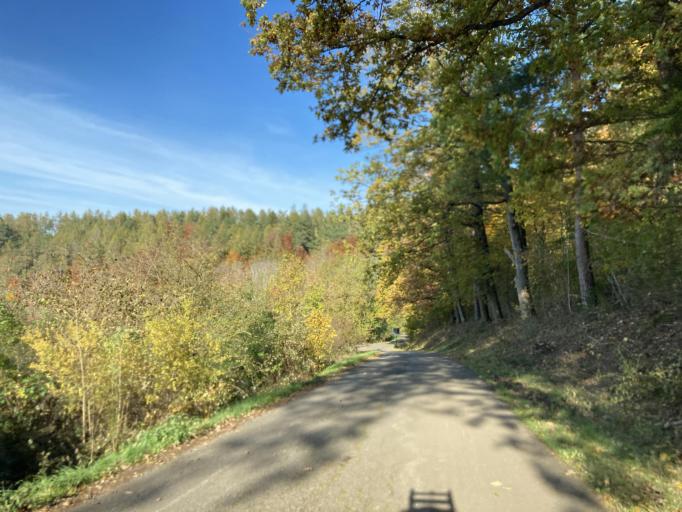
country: DE
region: Baden-Wuerttemberg
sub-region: Tuebingen Region
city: Mossingen
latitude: 48.3876
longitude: 9.0598
